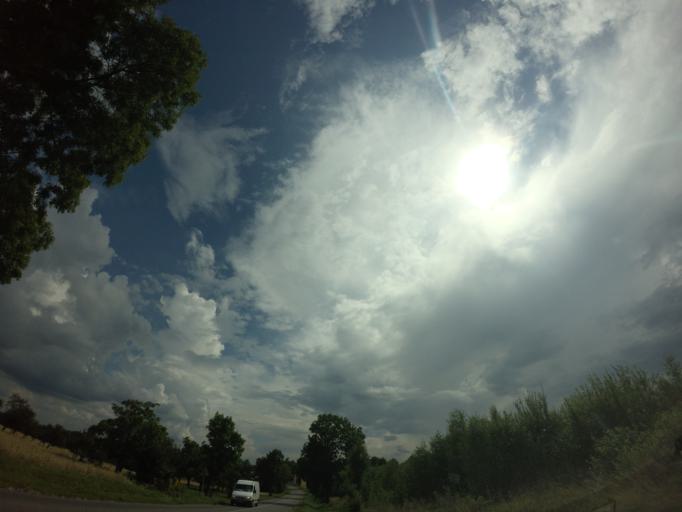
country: PL
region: Swietokrzyskie
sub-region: Powiat staszowski
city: Bogoria
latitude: 50.6937
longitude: 21.2382
